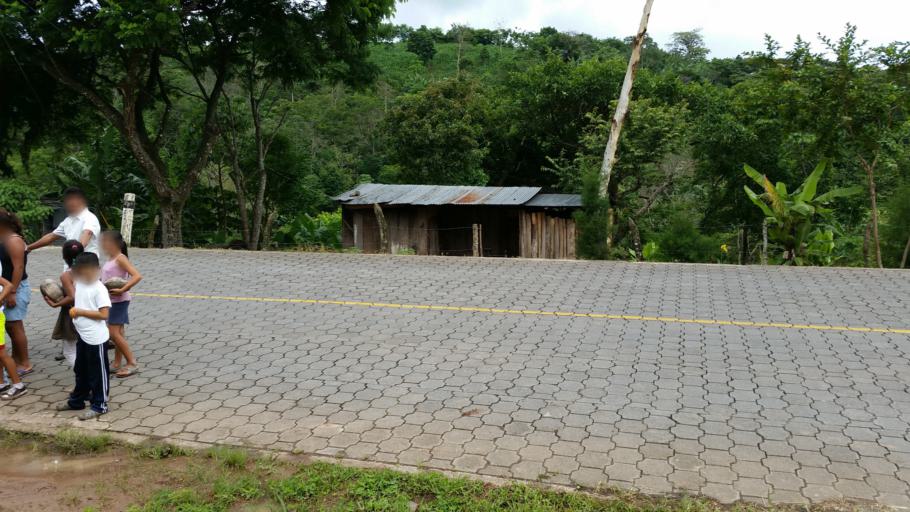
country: NI
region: Jinotega
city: Jinotega
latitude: 13.2092
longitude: -85.7172
